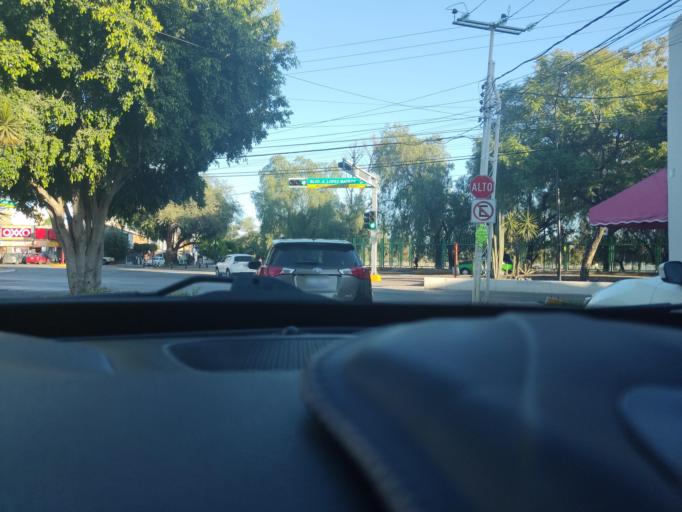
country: MX
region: Guanajuato
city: Leon
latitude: 21.1097
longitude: -101.6360
